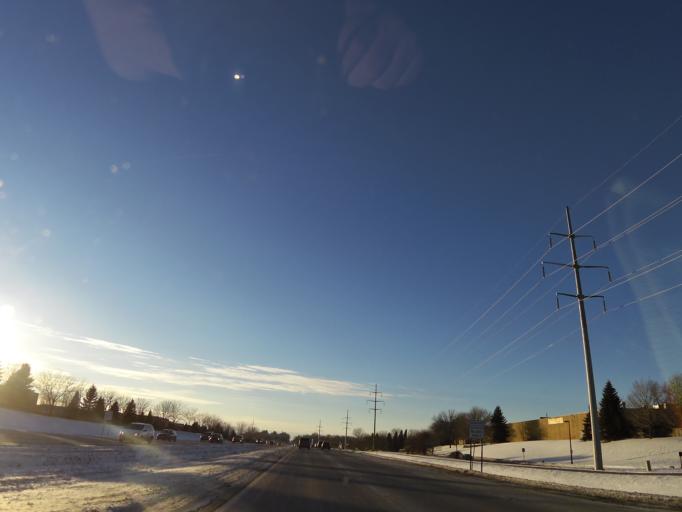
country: US
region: Minnesota
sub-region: Carver County
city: Chanhassen
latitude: 44.8623
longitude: -93.5148
